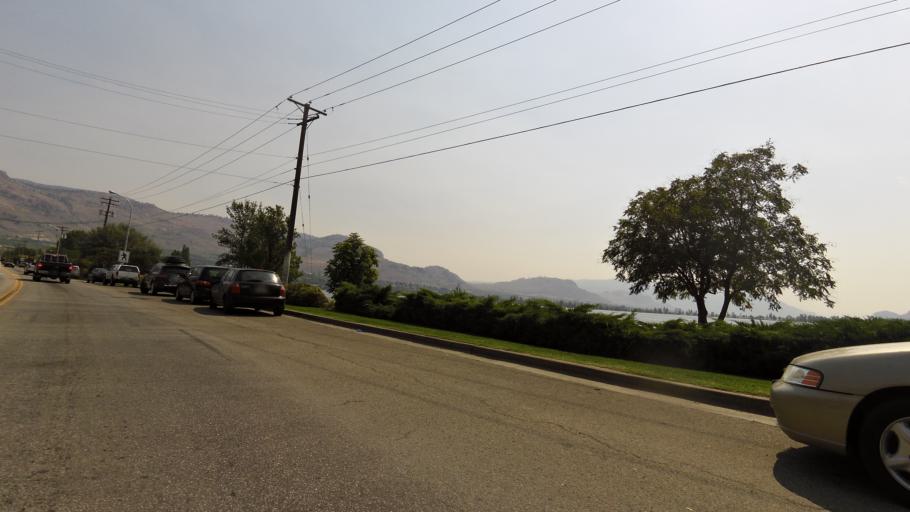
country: CA
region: British Columbia
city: Osoyoos
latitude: 49.0281
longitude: -119.4580
